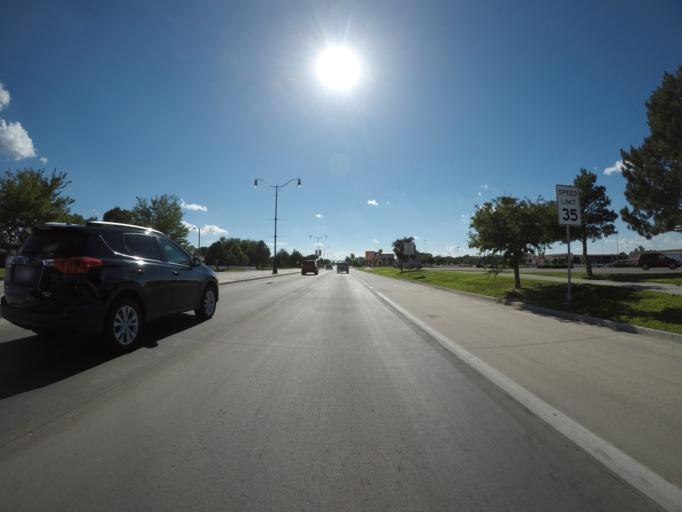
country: US
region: Colorado
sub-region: Logan County
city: Sterling
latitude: 40.6251
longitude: -103.2357
